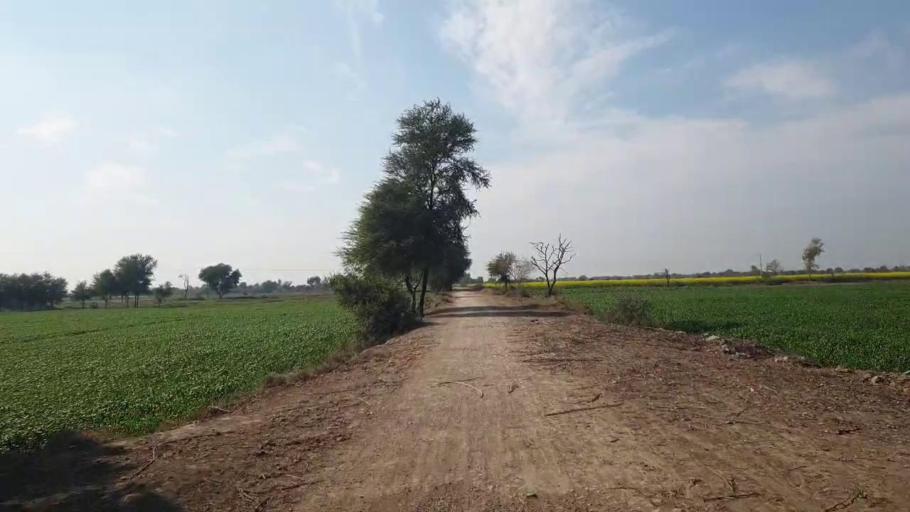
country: PK
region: Sindh
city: Shahdadpur
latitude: 25.9889
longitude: 68.5503
